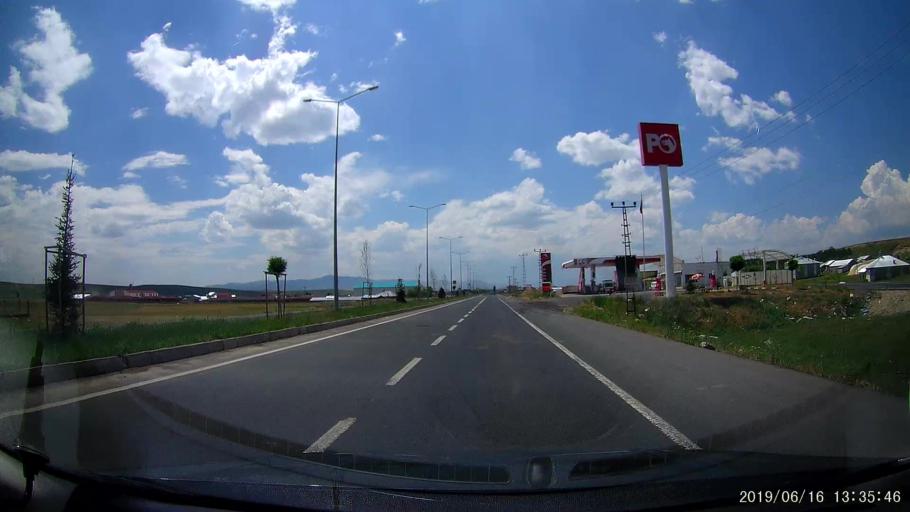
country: TR
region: Agri
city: Agri
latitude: 39.7128
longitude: 43.1080
